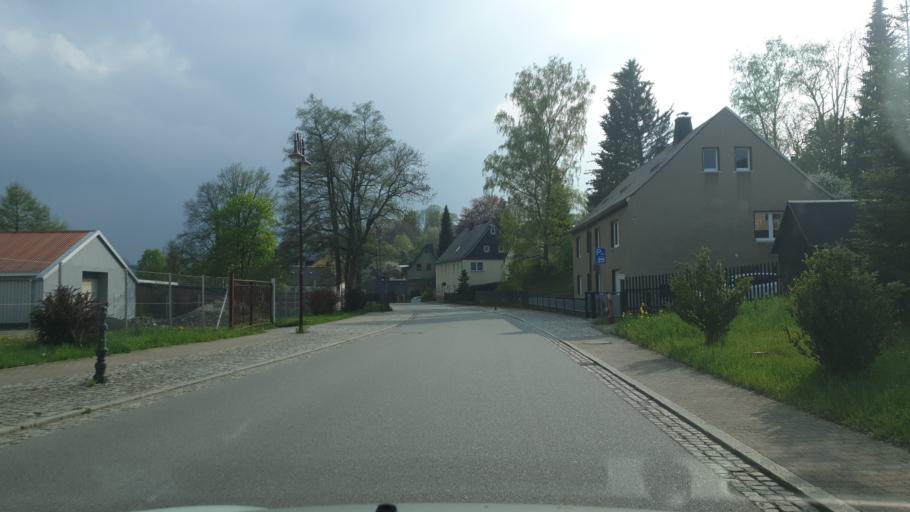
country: DE
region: Saxony
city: Lossnitz
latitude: 50.6284
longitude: 12.7366
